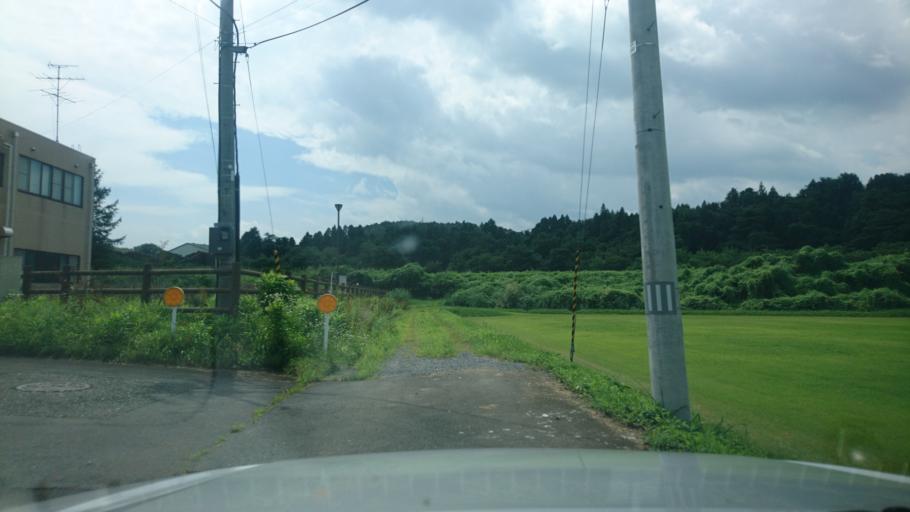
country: JP
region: Iwate
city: Ichinoseki
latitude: 38.8003
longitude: 140.9720
